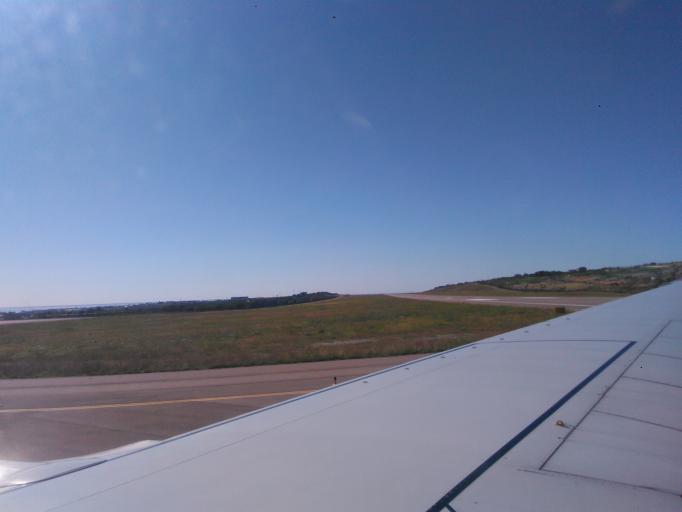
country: RU
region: Krasnodarskiy
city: Gelendzhik
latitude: 44.5949
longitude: 38.0184
